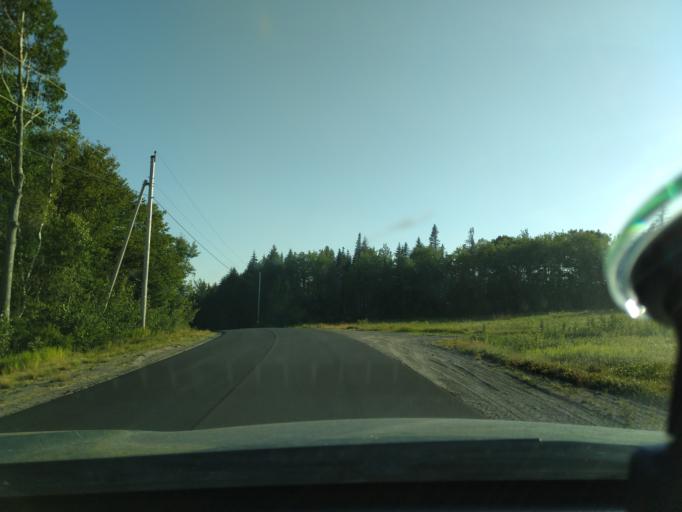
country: US
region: Maine
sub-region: Washington County
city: East Machias
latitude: 44.7054
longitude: -67.1503
